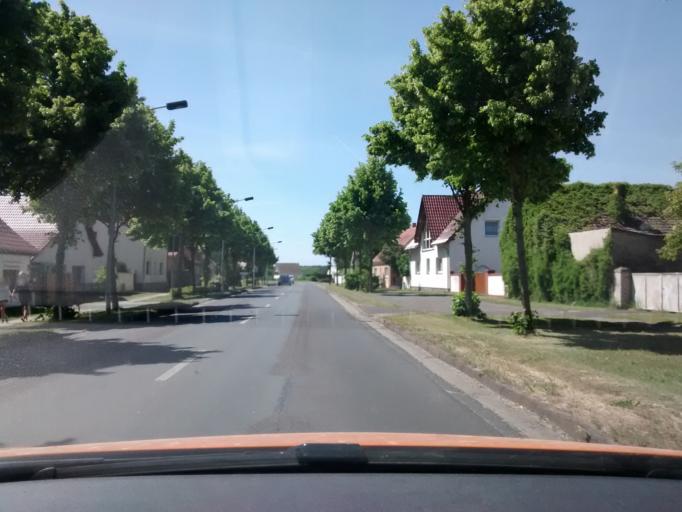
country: DE
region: Brandenburg
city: Storkow
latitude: 52.2831
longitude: 13.9056
